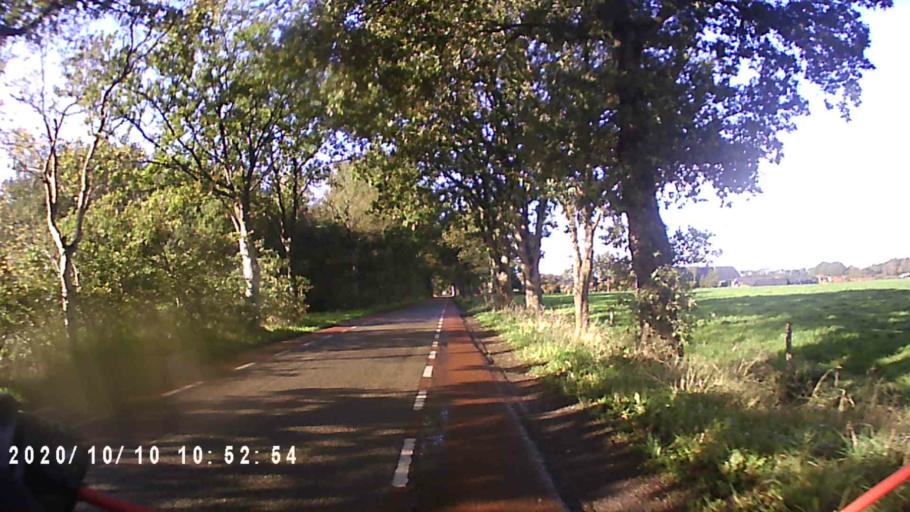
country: NL
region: Friesland
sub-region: Gemeente Achtkarspelen
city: Surhuisterveen
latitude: 53.1573
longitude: 6.2209
